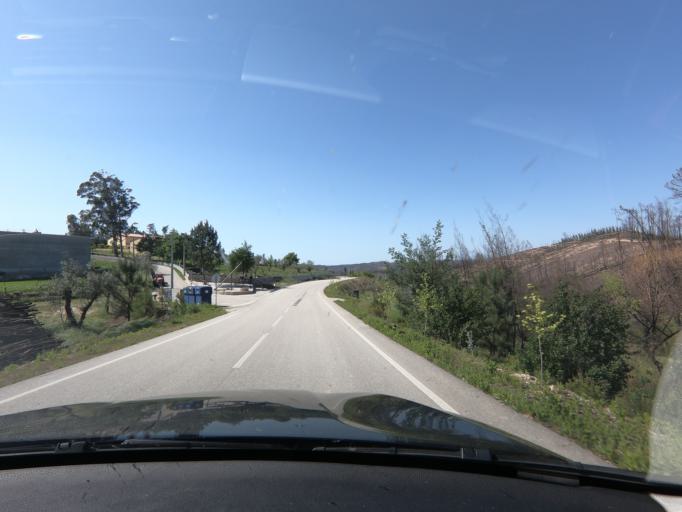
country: PT
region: Coimbra
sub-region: Penacova
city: Penacova
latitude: 40.2873
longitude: -8.2411
